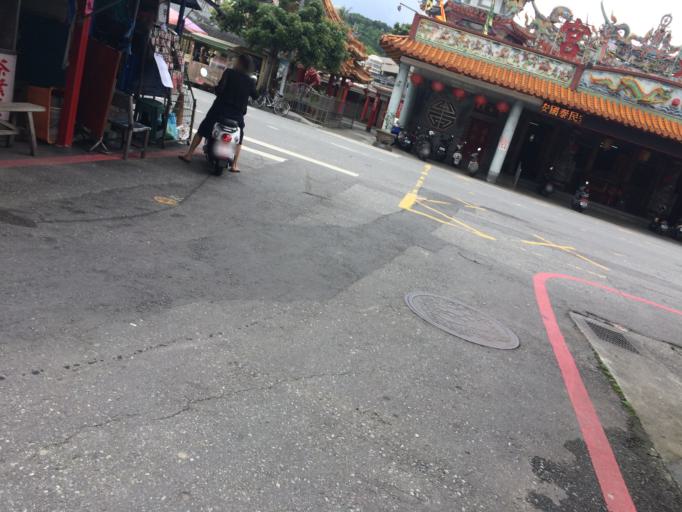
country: TW
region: Taiwan
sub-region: Hualien
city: Hualian
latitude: 23.9868
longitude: 121.6063
